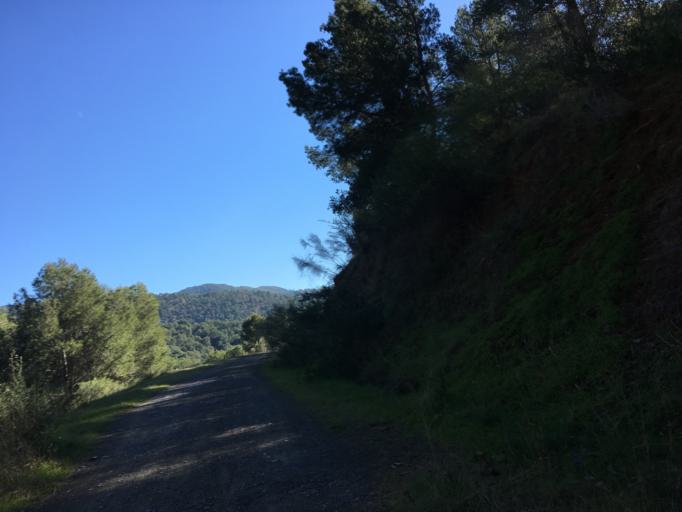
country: ES
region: Andalusia
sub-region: Provincia de Malaga
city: Malaga
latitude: 36.8010
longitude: -4.4076
